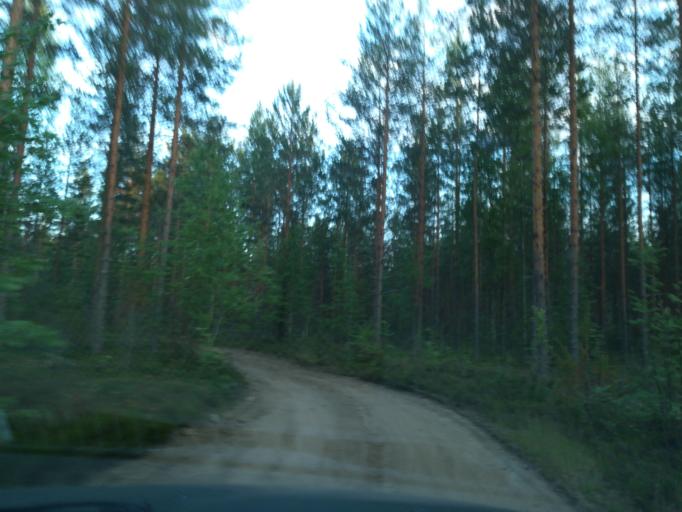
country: FI
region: South Karelia
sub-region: Lappeenranta
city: Joutseno
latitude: 61.3429
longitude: 28.4029
